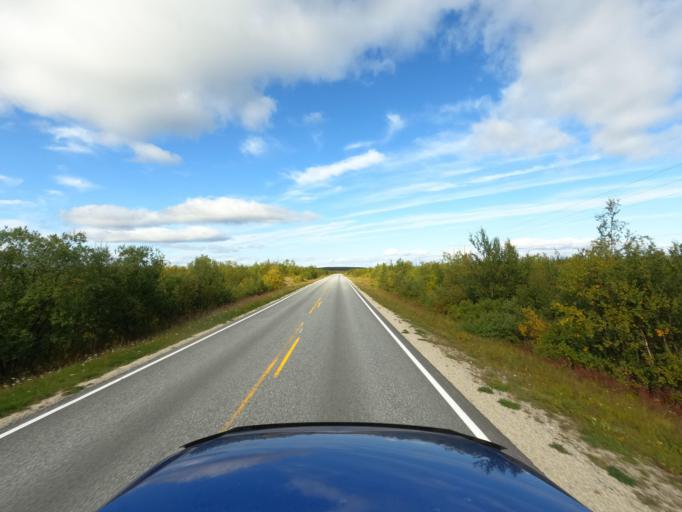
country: NO
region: Finnmark Fylke
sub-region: Karasjok
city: Karasjohka
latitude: 69.6660
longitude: 25.2742
